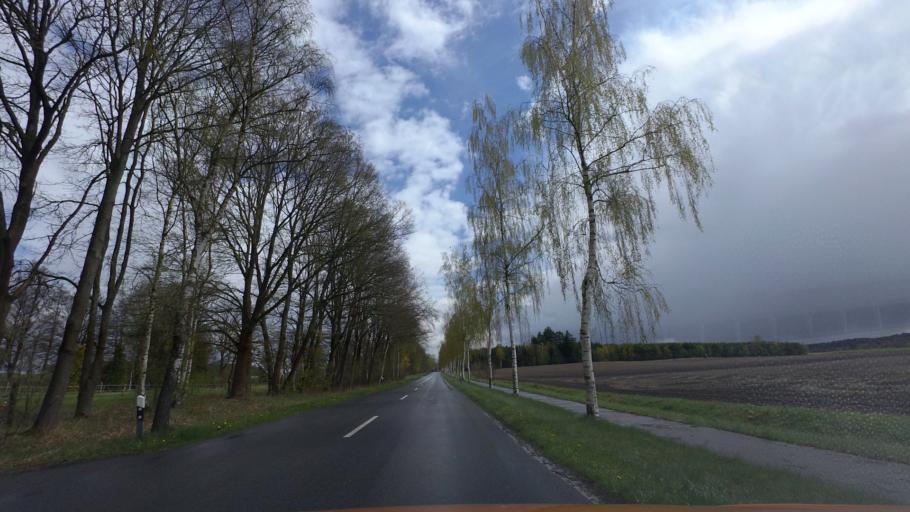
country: DE
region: Lower Saxony
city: Oldendorf
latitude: 53.1774
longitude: 10.2211
